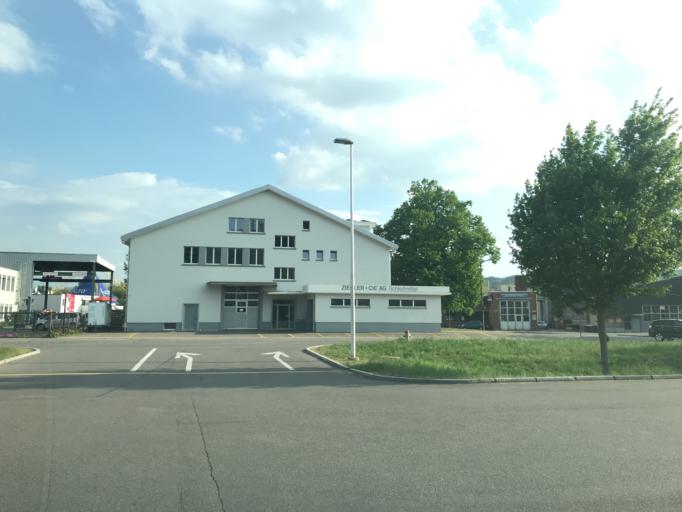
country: CH
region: Zurich
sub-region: Bezirk Winterthur
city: Mattenbach (Kreis 7) / Gutschick
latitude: 47.4968
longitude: 8.7528
